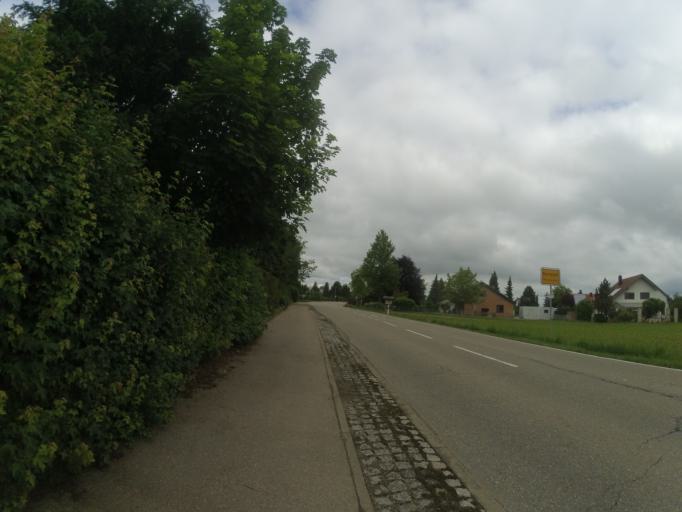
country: DE
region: Baden-Wuerttemberg
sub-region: Tuebingen Region
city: Bernstadt
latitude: 48.4944
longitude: 10.0271
